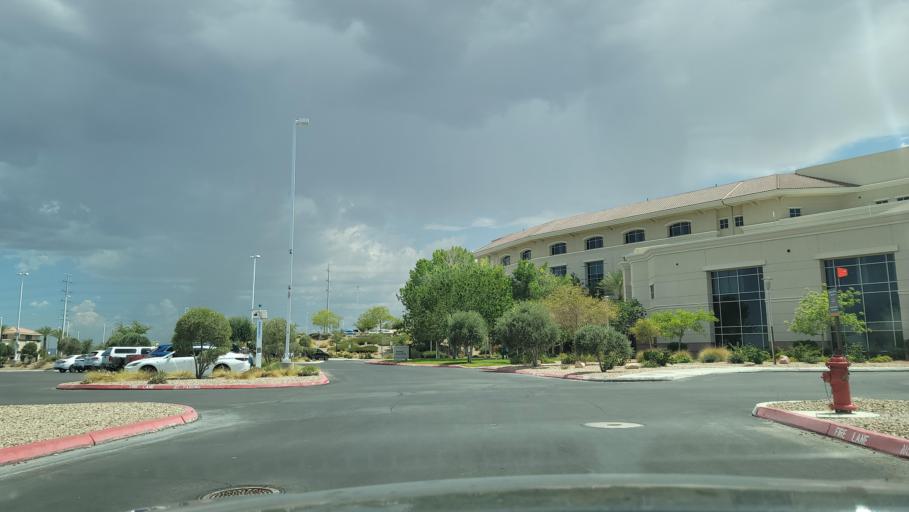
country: US
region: Nevada
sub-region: Clark County
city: Enterprise
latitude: 36.0581
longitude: -115.2714
